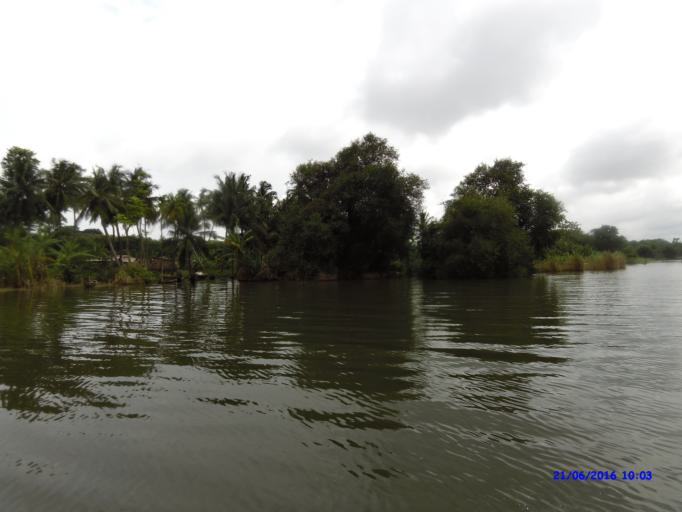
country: BJ
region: Mono
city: Come
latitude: 6.4556
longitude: 1.9253
